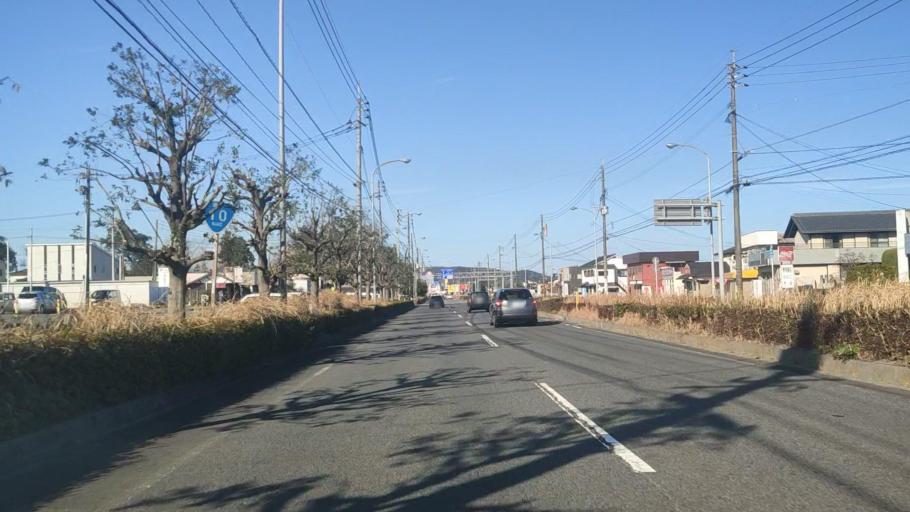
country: JP
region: Oita
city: Oita
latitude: 33.1445
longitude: 131.6578
